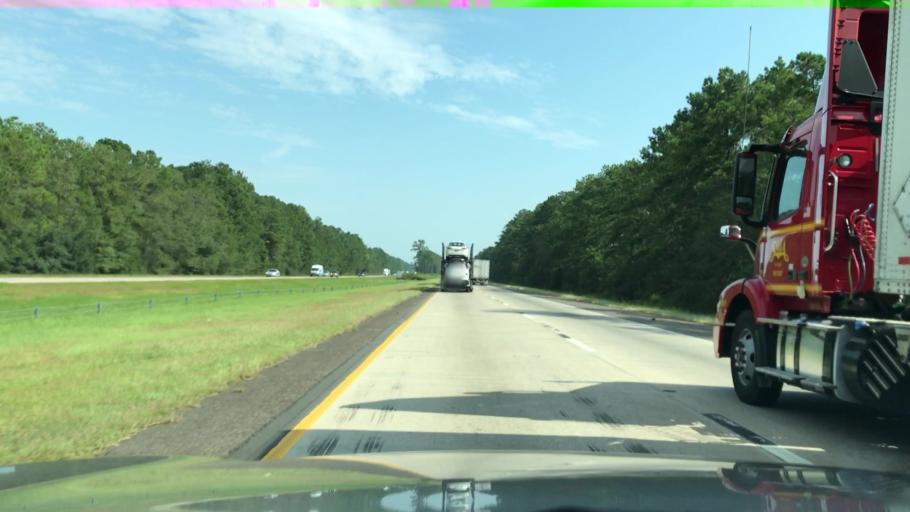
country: US
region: South Carolina
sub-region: Colleton County
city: Walterboro
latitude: 32.8416
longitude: -80.7391
